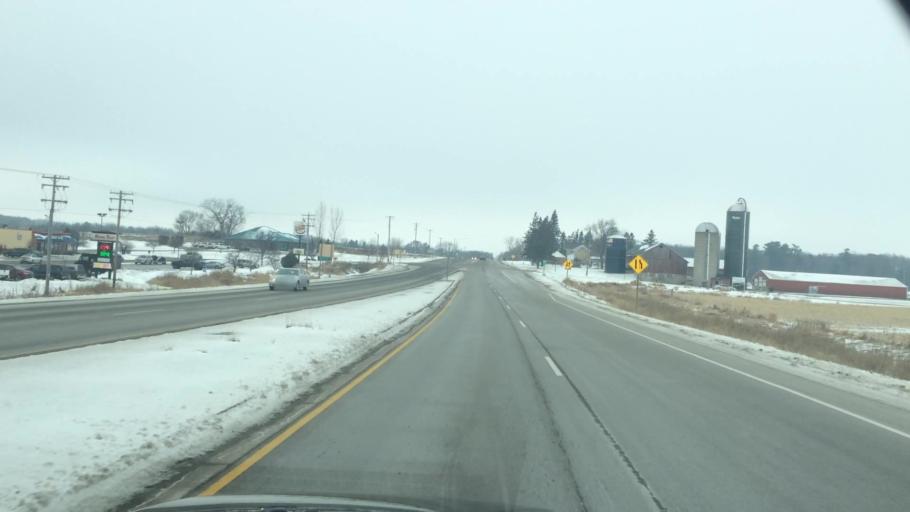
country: US
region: Wisconsin
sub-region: Shawano County
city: Bonduel
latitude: 44.7291
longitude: -88.4456
